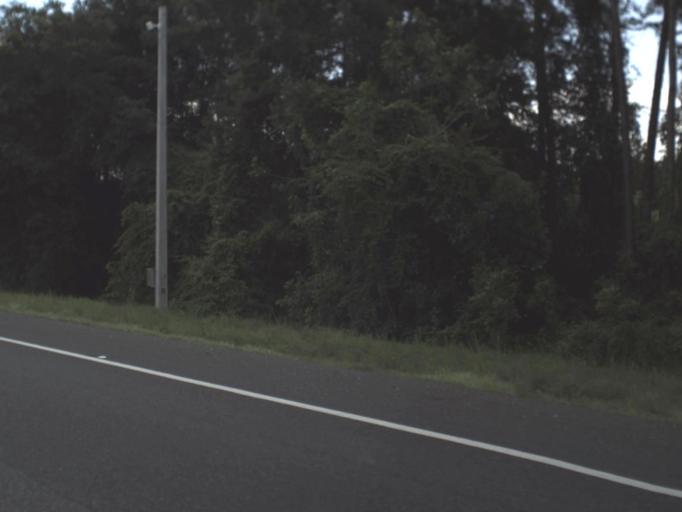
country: US
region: Florida
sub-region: Duval County
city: Jacksonville
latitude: 30.4450
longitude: -81.6048
